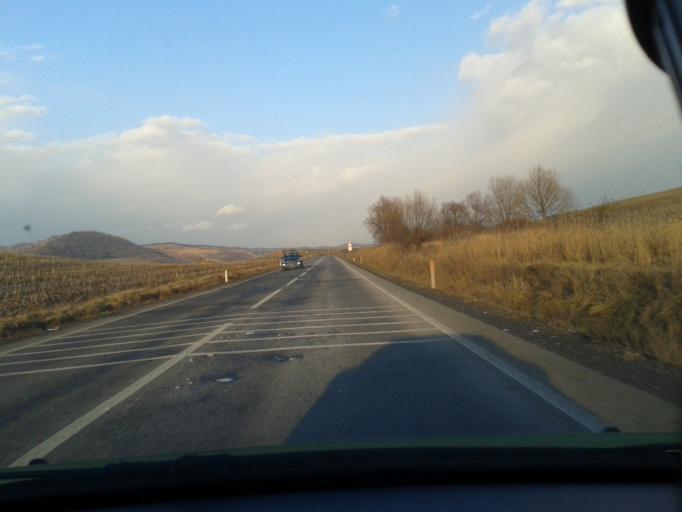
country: RO
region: Sibiu
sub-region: Comuna Tarnava
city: Tarnava
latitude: 46.1231
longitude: 24.2841
